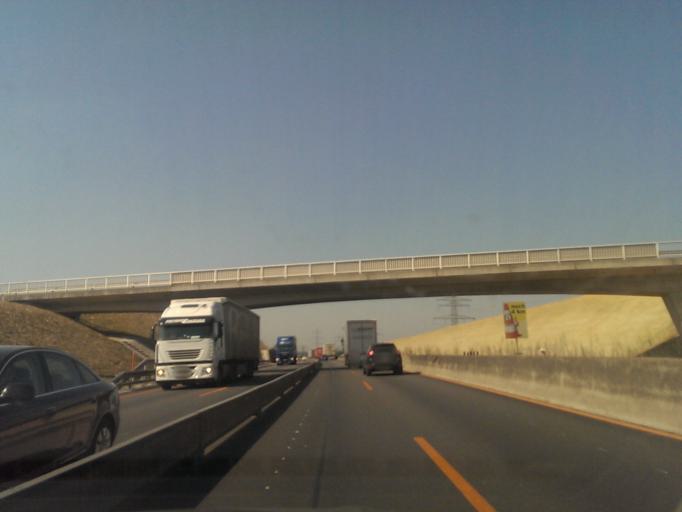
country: AT
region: Upper Austria
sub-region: Politischer Bezirk Vocklabruck
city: Wolfsegg am Hausruck
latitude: 48.1854
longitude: 13.6869
